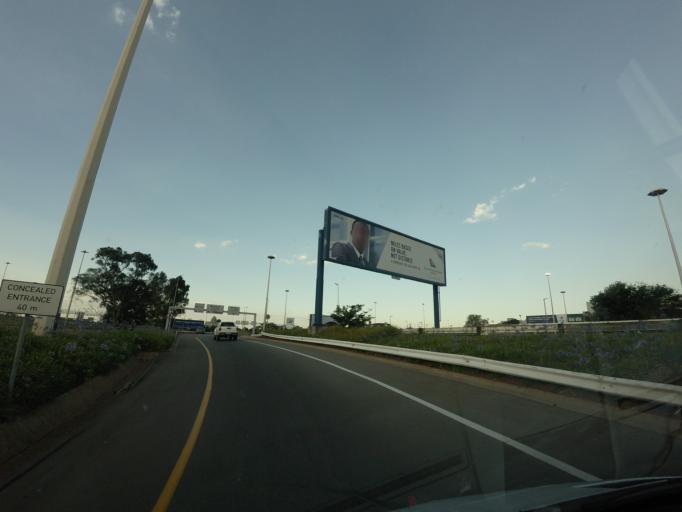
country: ZA
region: Gauteng
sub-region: City of Johannesburg Metropolitan Municipality
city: Modderfontein
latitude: -26.1312
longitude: 28.2288
